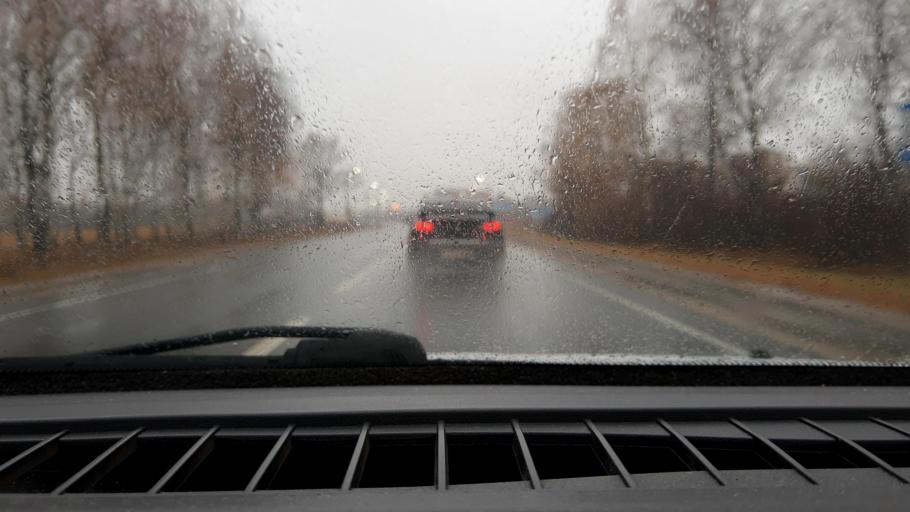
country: RU
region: Nizjnij Novgorod
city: Sitniki
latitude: 56.5094
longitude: 44.0235
